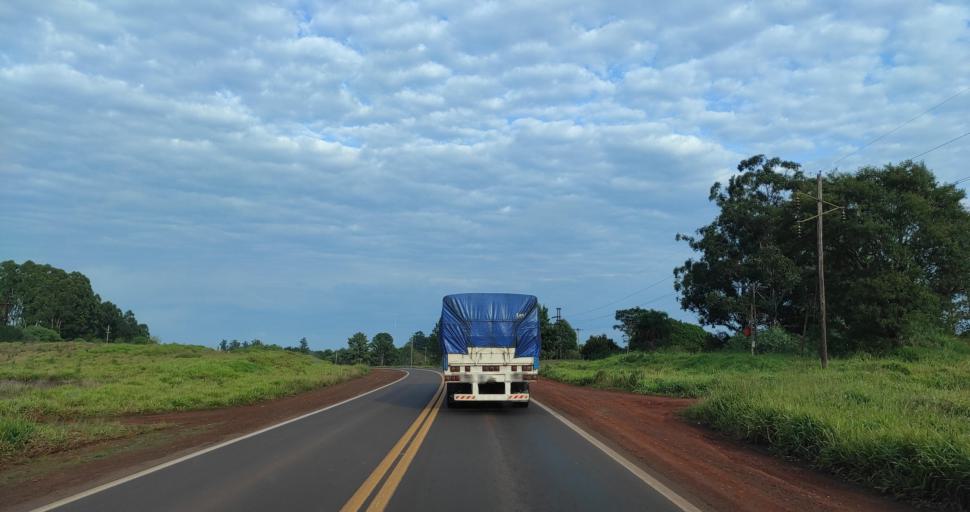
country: AR
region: Corrientes
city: Gobernador Ingeniero Valentin Virasoro
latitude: -27.9395
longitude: -55.9800
